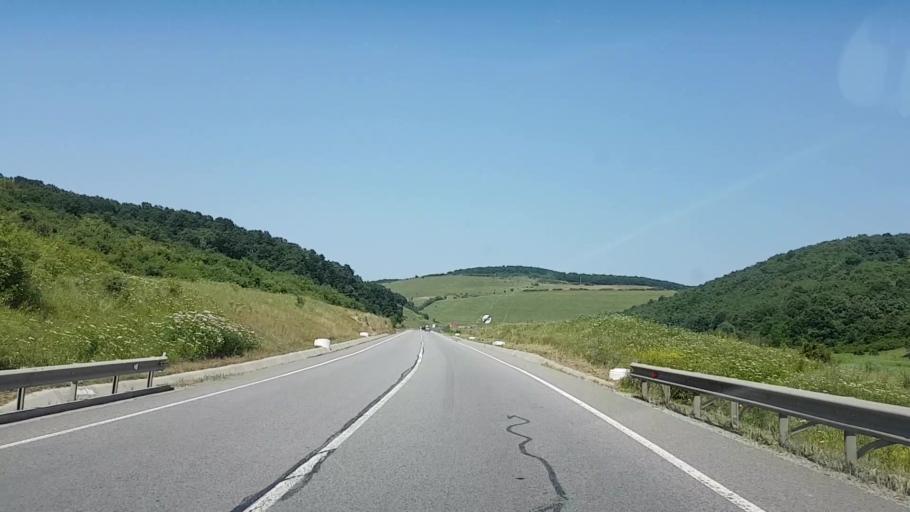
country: RO
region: Cluj
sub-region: Comuna Feleacu
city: Gheorghieni
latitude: 46.7347
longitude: 23.7061
